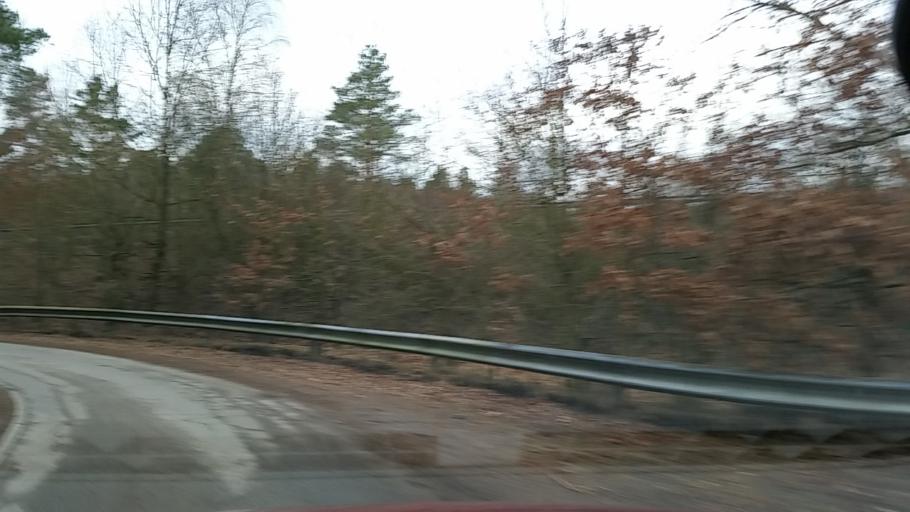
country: DE
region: Lower Saxony
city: Wieren
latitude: 52.8775
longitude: 10.6421
